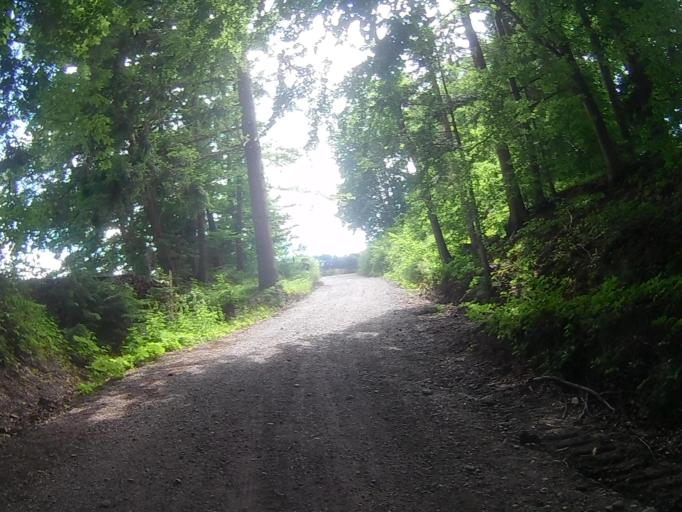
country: SI
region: Ruse
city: Ruse
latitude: 46.5197
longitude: 15.5221
